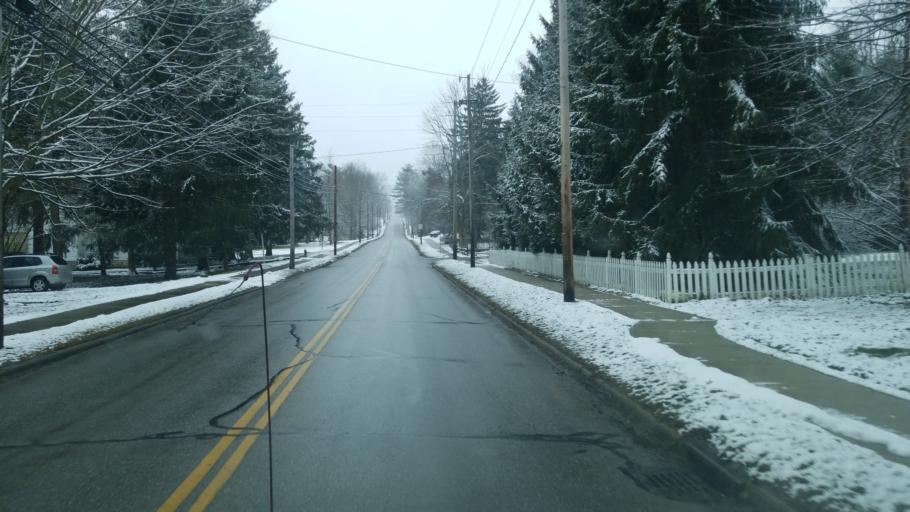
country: US
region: Ohio
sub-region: Portage County
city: Hiram
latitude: 41.3095
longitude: -81.1465
